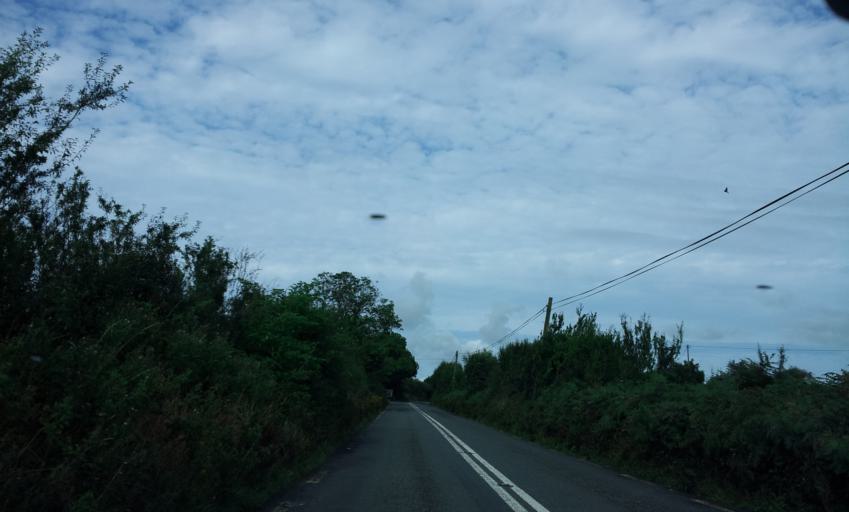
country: IE
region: Munster
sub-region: Ciarrai
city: Killorglin
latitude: 52.0829
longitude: -9.6692
